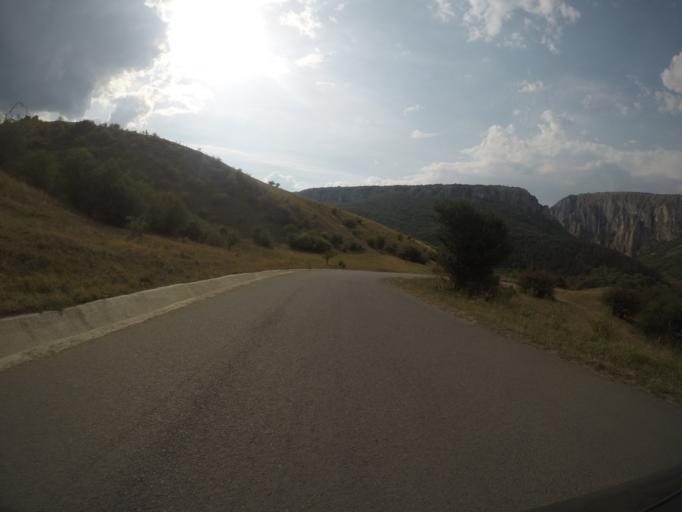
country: RO
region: Cluj
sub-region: Comuna Sandulesti
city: Sandulesti
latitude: 46.5574
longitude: 23.6950
